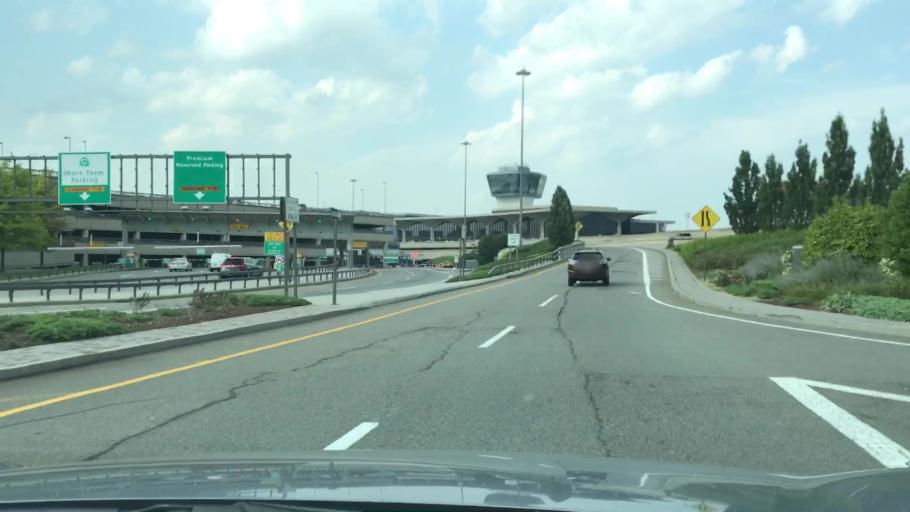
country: US
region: New Jersey
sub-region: Union County
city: Elizabeth
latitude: 40.6919
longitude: -74.1777
